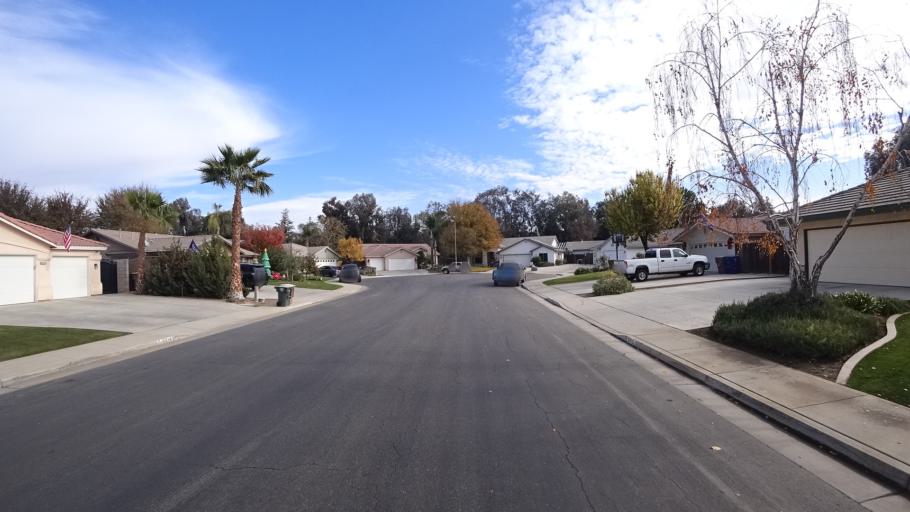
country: US
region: California
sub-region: Kern County
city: Greenacres
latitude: 35.3990
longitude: -119.0769
